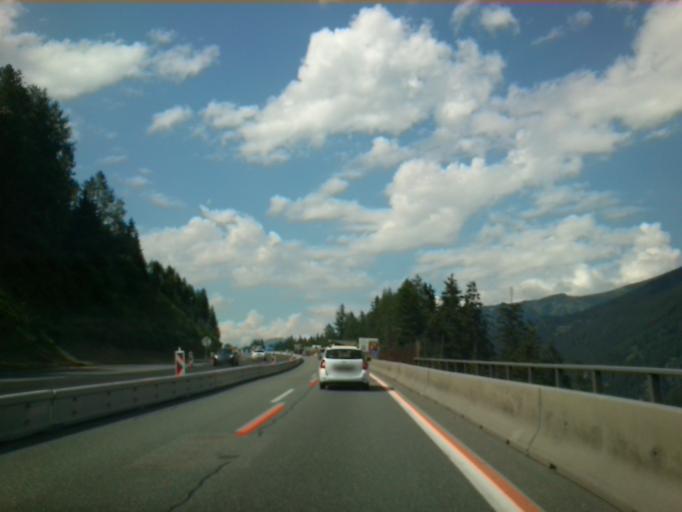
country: AT
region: Tyrol
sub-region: Politischer Bezirk Innsbruck Land
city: Gries am Brenner
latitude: 47.0496
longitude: 11.4816
